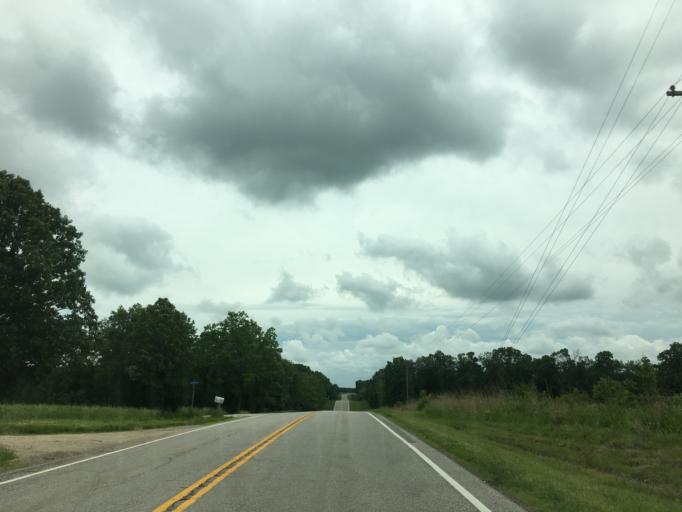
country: US
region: Missouri
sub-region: Gasconade County
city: Owensville
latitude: 38.4897
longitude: -91.4620
